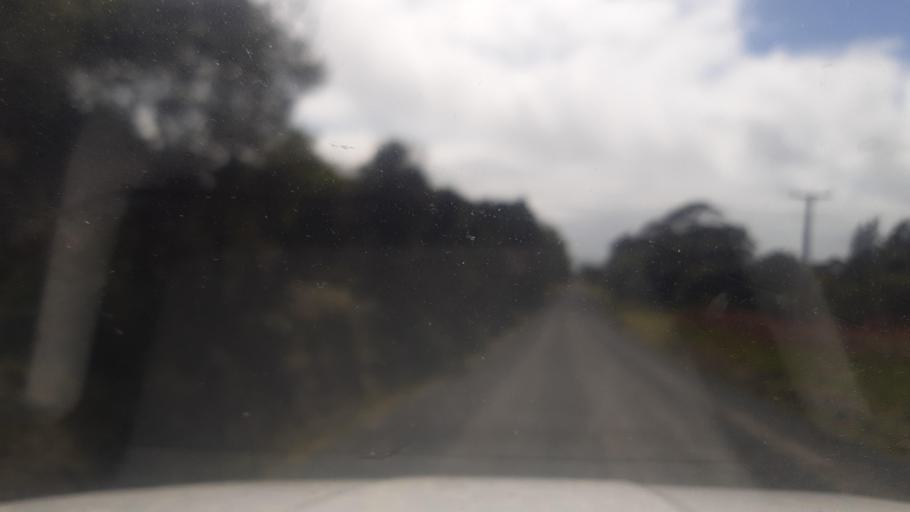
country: NZ
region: Northland
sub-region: Far North District
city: Kaitaia
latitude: -34.7434
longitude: 173.1060
